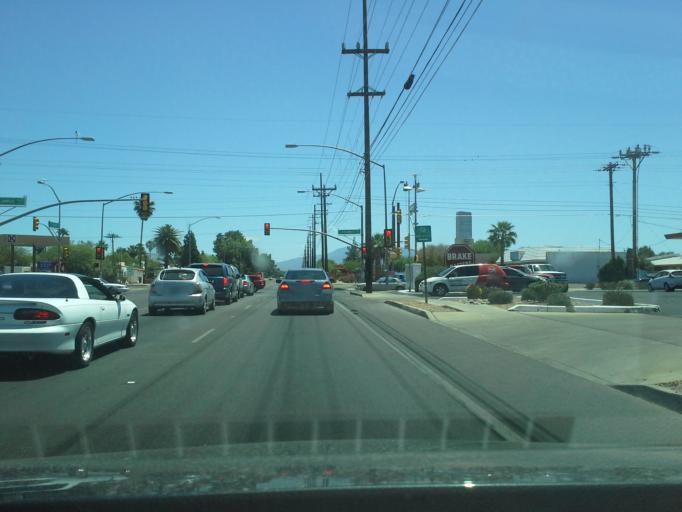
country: US
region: Arizona
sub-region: Pima County
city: Tucson
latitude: 32.2505
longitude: -110.9019
